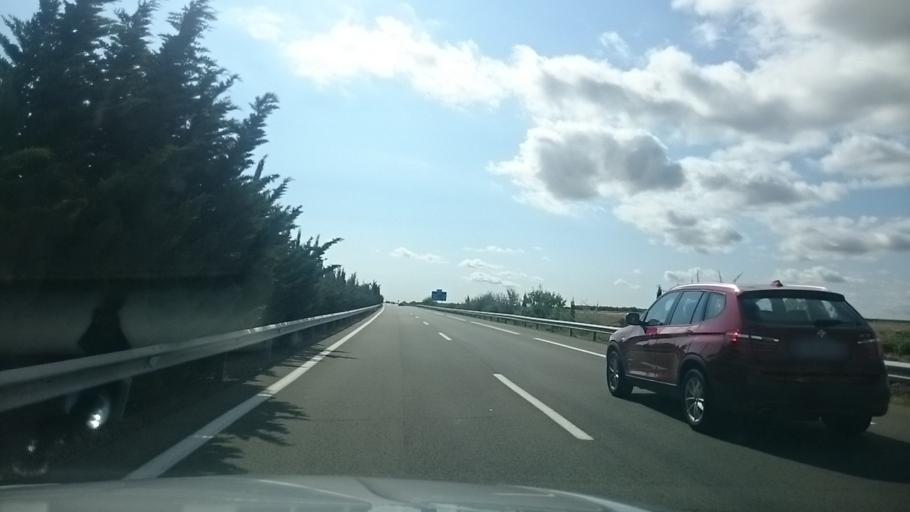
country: ES
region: La Rioja
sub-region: Provincia de La Rioja
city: Aldeanueva de Ebro
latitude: 42.2126
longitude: -1.8817
